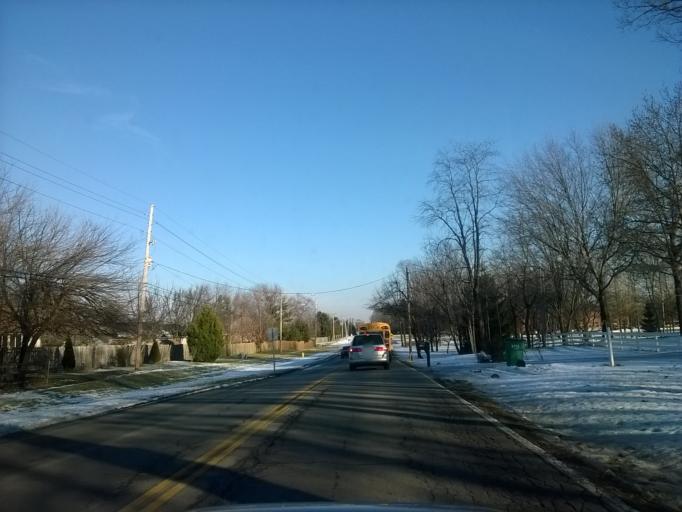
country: US
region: Indiana
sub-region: Hamilton County
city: Carmel
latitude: 39.9784
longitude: -86.0844
